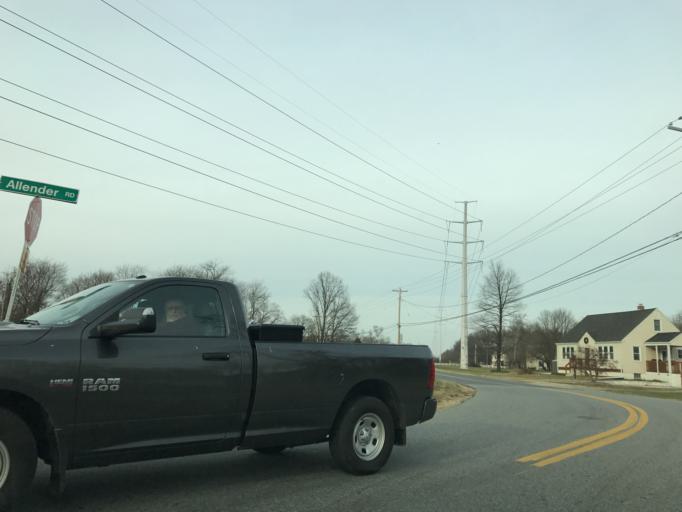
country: US
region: Maryland
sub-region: Baltimore County
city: White Marsh
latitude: 39.4030
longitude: -76.4085
